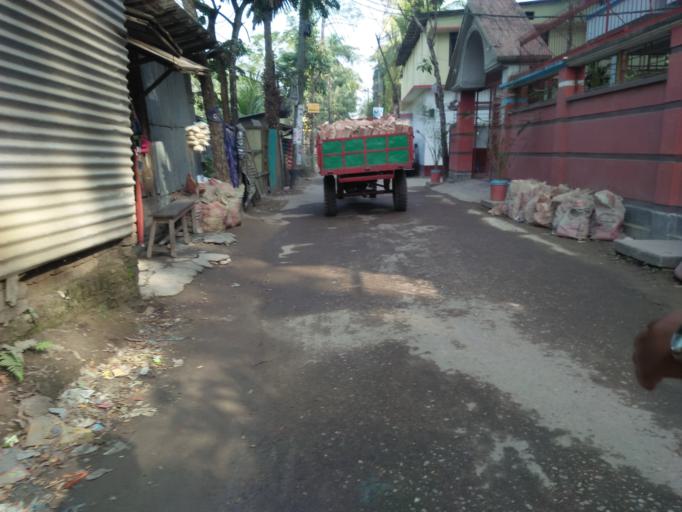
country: BD
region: Barisal
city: Bhola
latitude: 22.6814
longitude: 90.6426
